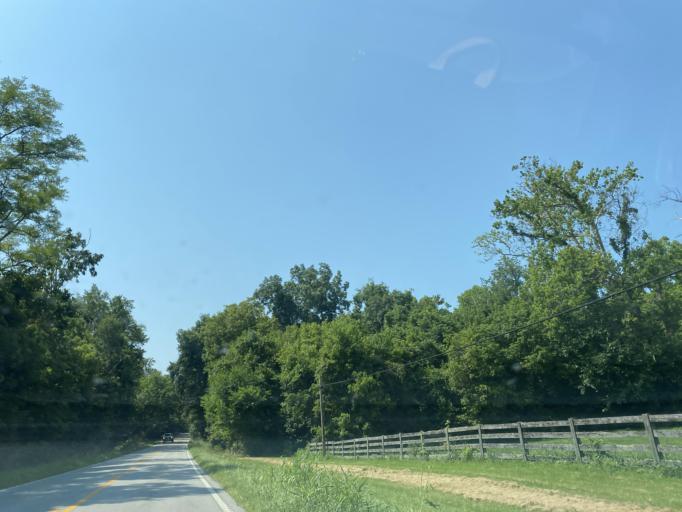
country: US
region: Kentucky
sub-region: Campbell County
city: Claryville
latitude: 38.8998
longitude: -84.4451
